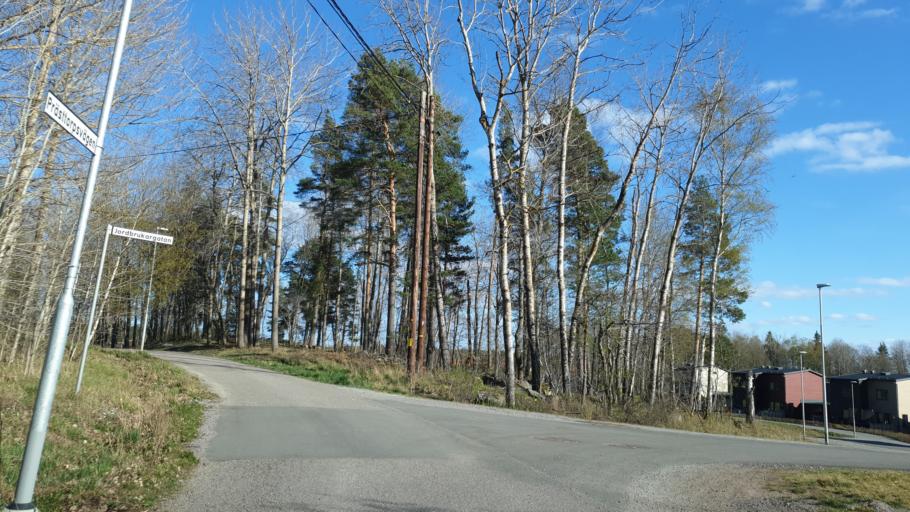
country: SE
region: Stockholm
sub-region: Upplands Vasby Kommun
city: Upplands Vaesby
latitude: 59.5174
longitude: 17.8770
